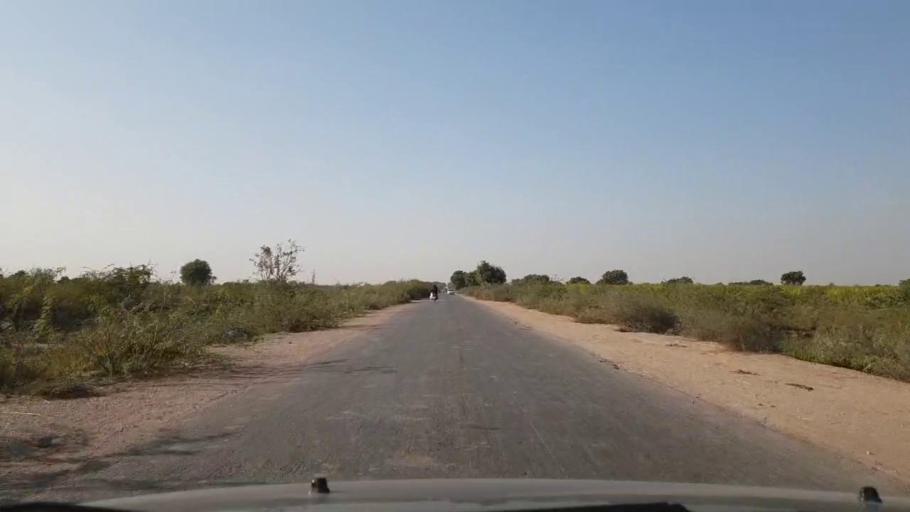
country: PK
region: Sindh
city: Tando Ghulam Ali
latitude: 25.1452
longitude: 68.8667
